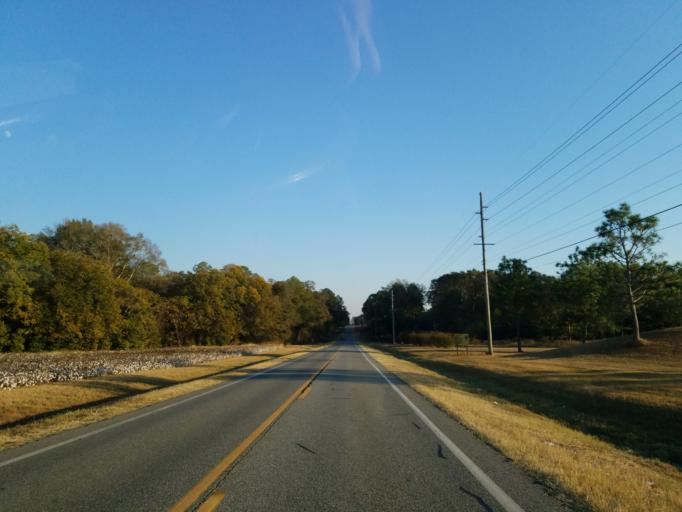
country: US
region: Georgia
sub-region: Crisp County
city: Cordele
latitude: 31.9397
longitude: -83.7356
